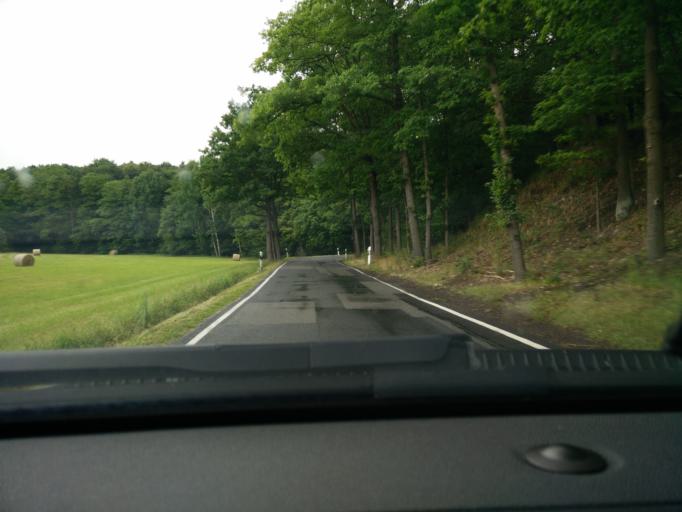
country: DE
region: Saxony
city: Grossbardau
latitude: 51.1649
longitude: 12.7020
